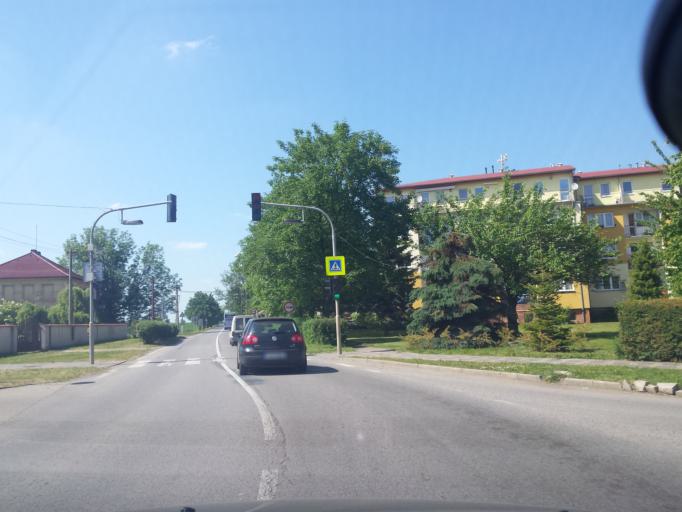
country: CZ
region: Central Bohemia
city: Velke Prilepy
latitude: 50.1913
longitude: 14.3222
